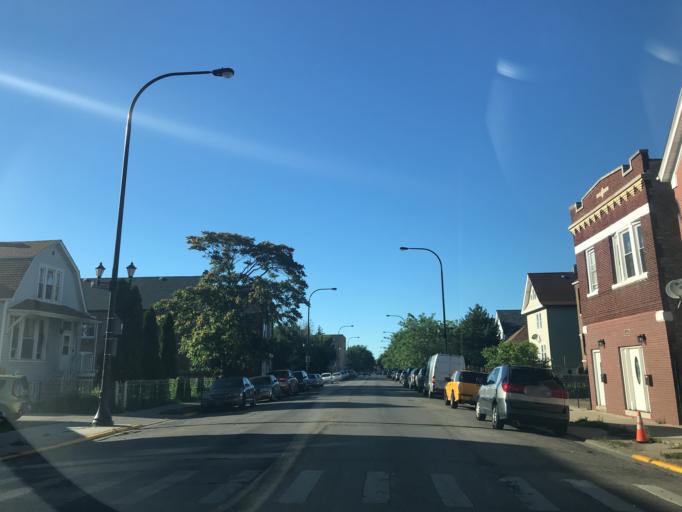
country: US
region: Illinois
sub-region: Cook County
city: Cicero
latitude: 41.8600
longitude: -87.7495
